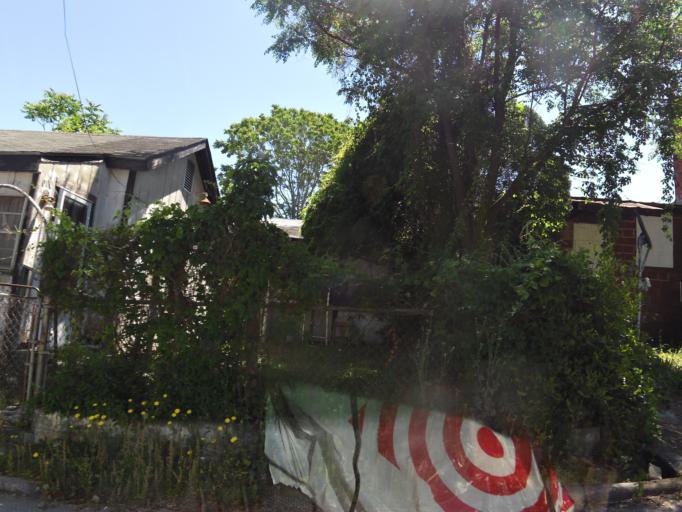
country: US
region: Georgia
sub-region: Richmond County
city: Augusta
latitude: 33.4828
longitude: -82.0224
